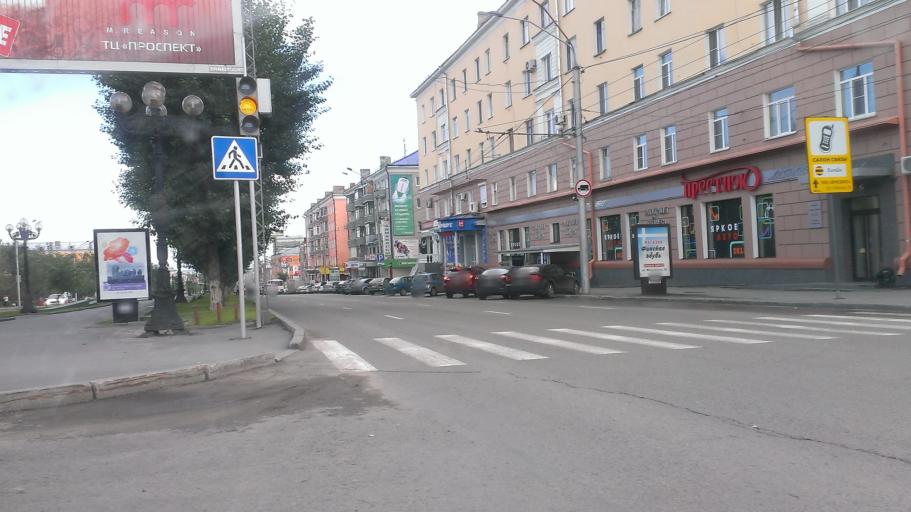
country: RU
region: Altai Krai
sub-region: Gorod Barnaulskiy
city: Barnaul
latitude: 53.3456
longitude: 83.7794
